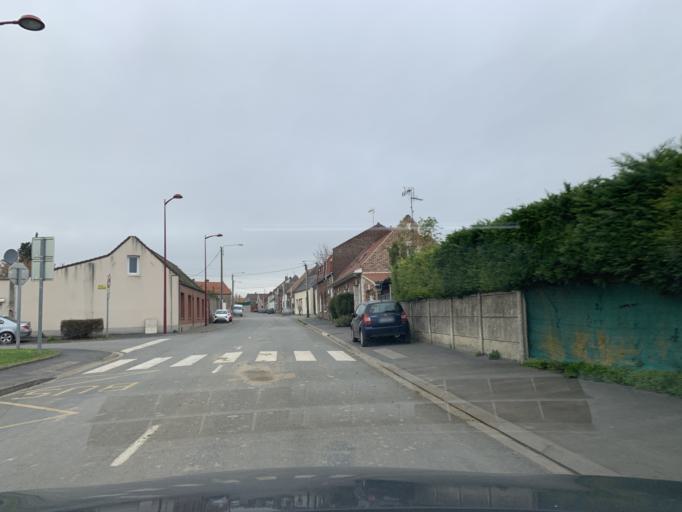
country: FR
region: Nord-Pas-de-Calais
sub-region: Departement du Pas-de-Calais
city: Oisy-le-Verger
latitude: 50.2488
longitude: 3.1284
